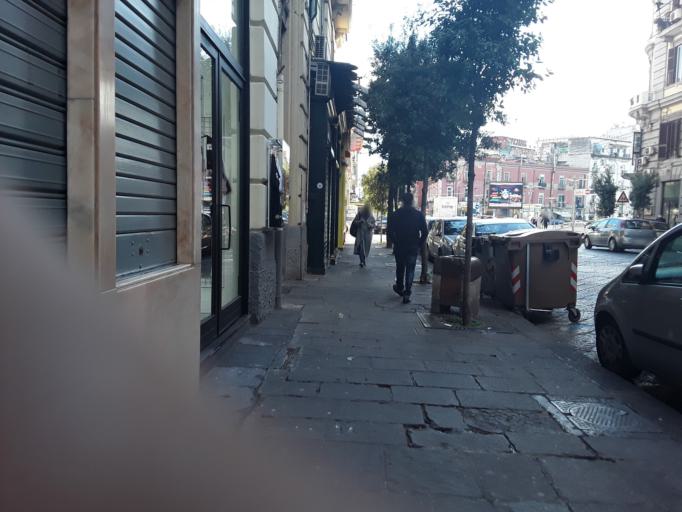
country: IT
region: Campania
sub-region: Provincia di Napoli
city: Napoli
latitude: 40.8564
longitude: 14.2674
